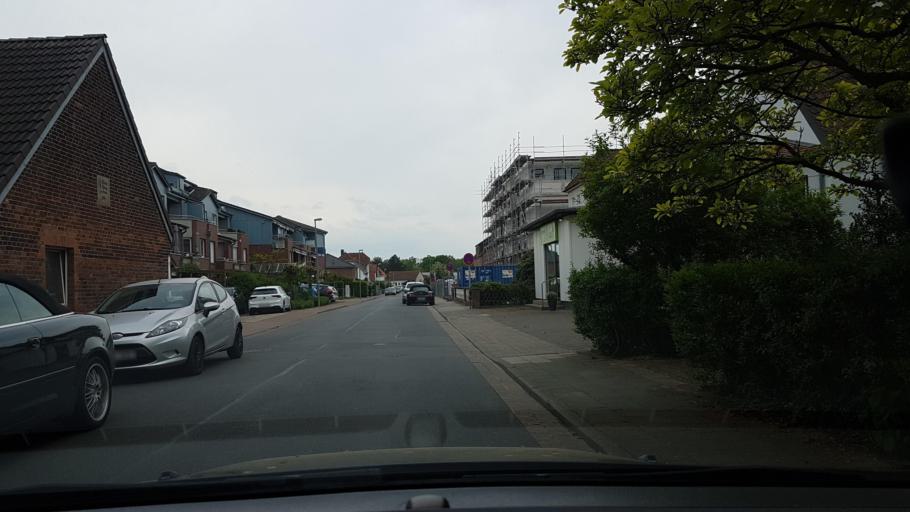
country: DE
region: Lower Saxony
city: Garbsen-Mitte
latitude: 52.4355
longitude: 9.6070
